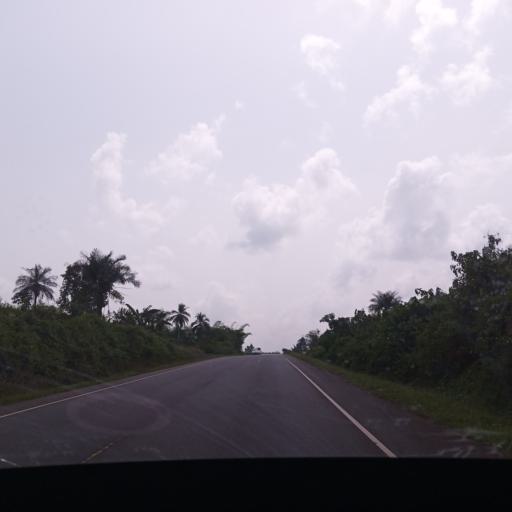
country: LR
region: Margibi
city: Kakata
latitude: 6.2386
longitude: -10.2843
